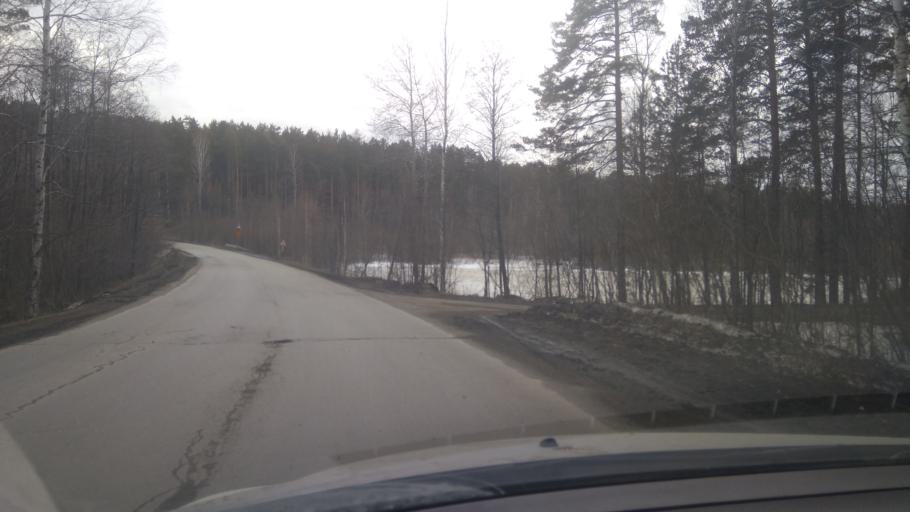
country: RU
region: Sverdlovsk
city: Severka
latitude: 56.8365
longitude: 60.3823
